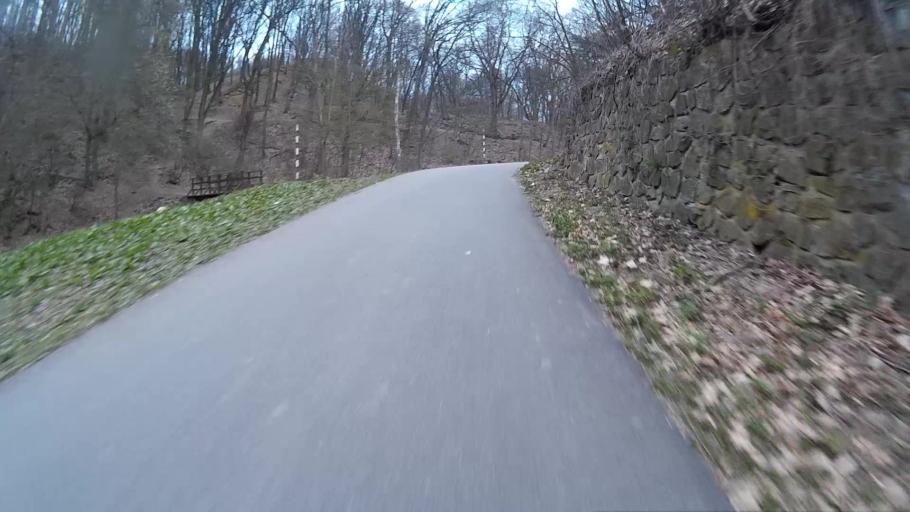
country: CZ
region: South Moravian
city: Ostopovice
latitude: 49.1842
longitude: 16.5674
